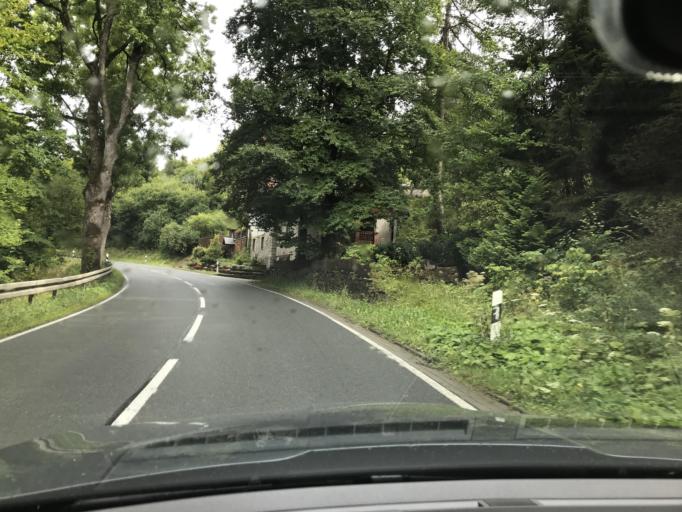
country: DE
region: Saxony-Anhalt
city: Rubeland
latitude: 51.7622
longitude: 10.8691
